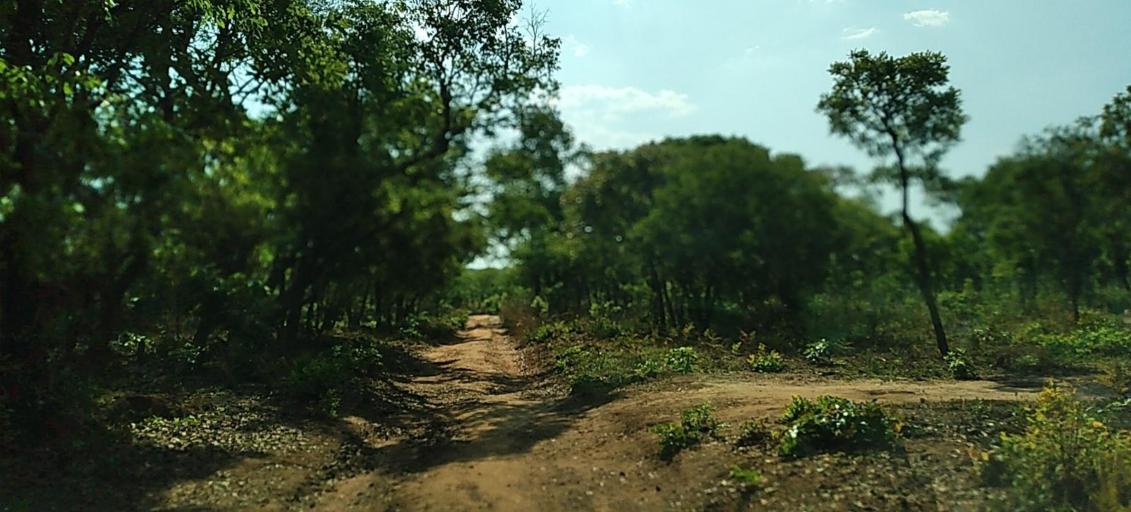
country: ZM
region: North-Western
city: Mwinilunga
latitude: -11.2981
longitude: 24.8636
